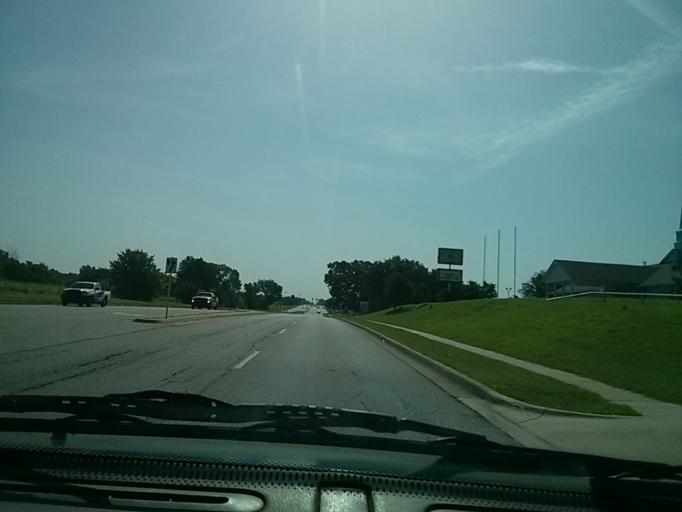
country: US
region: Oklahoma
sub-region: Tulsa County
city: Broken Arrow
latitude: 36.1334
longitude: -95.8272
